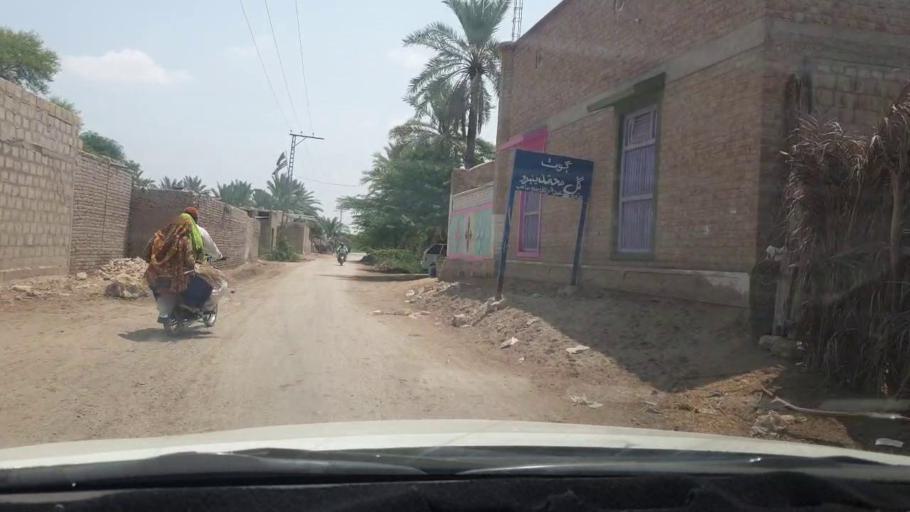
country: PK
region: Sindh
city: Khairpur
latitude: 27.5355
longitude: 68.8851
